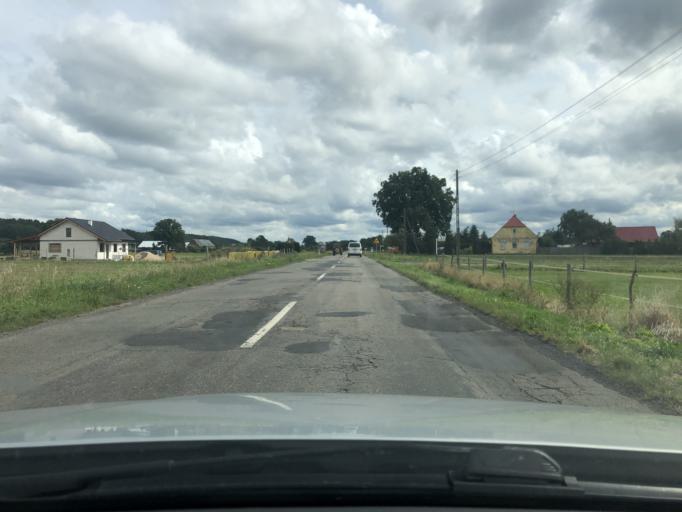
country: PL
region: Lubusz
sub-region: Powiat strzelecko-drezdenecki
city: Drezdenko
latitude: 52.8429
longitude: 15.8851
